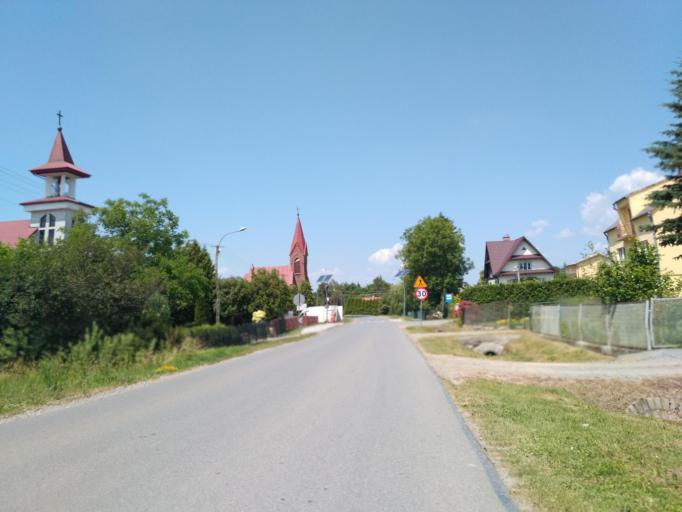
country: PL
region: Subcarpathian Voivodeship
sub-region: Powiat sanocki
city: Niebieszczany
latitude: 49.5217
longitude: 22.1311
